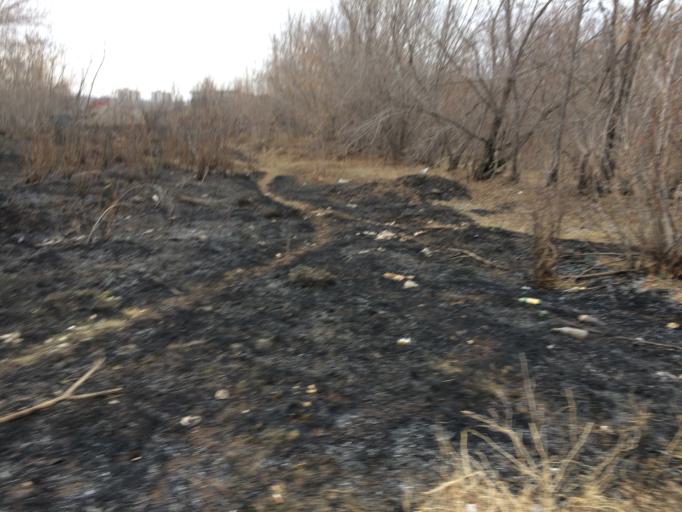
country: RU
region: Chelyabinsk
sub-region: Gorod Magnitogorsk
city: Magnitogorsk
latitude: 53.4396
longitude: 58.9769
